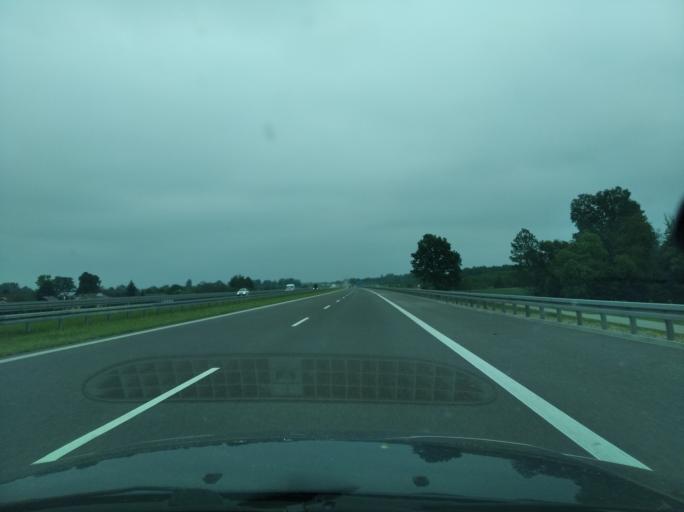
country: PL
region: Subcarpathian Voivodeship
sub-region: Powiat lancucki
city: Czarna
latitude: 50.0908
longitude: 22.1890
